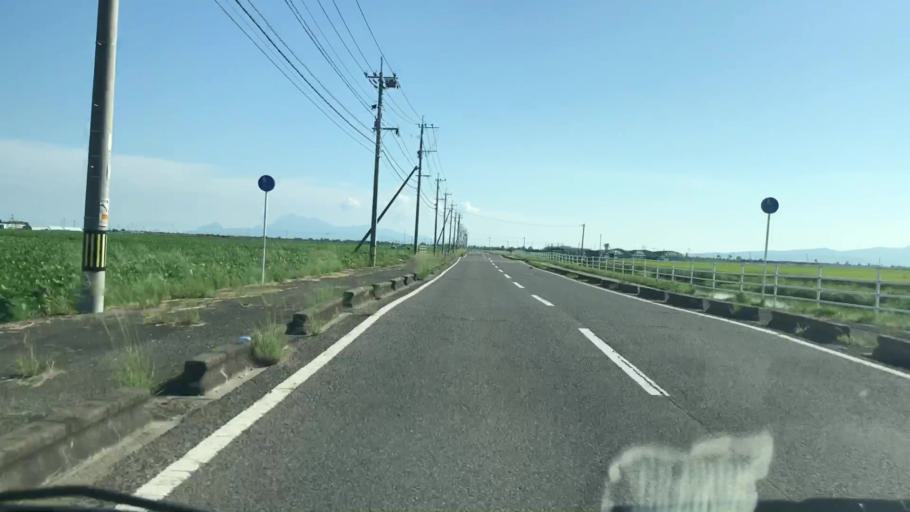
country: JP
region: Saga Prefecture
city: Okawa
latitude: 33.1720
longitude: 130.3108
